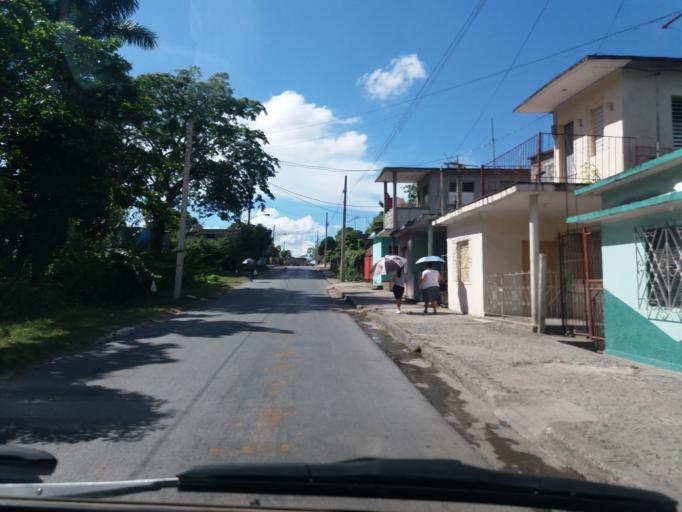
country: CU
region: Cienfuegos
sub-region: Municipio de Cienfuegos
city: Cienfuegos
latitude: 22.1484
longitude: -80.4263
